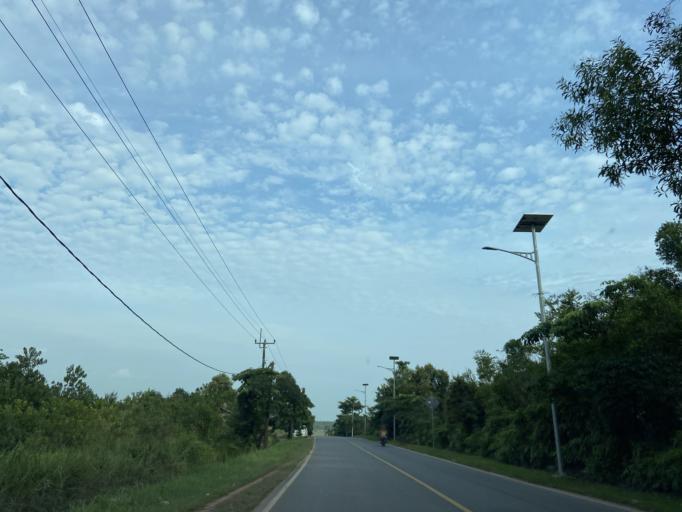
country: ID
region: Riau Islands
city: Tanjungpinang
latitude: 0.9343
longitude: 104.1078
